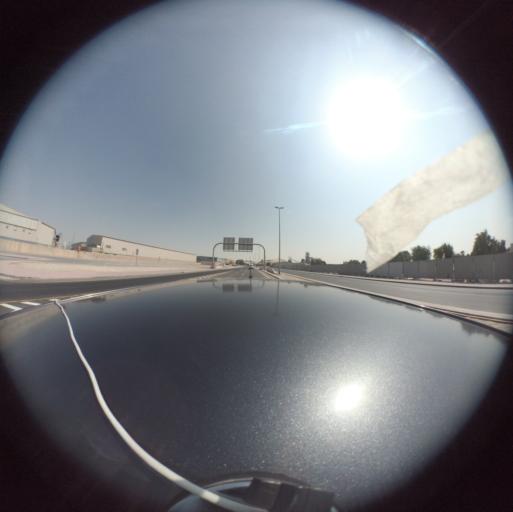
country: AE
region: Dubai
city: Dubai
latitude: 25.1622
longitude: 55.2382
